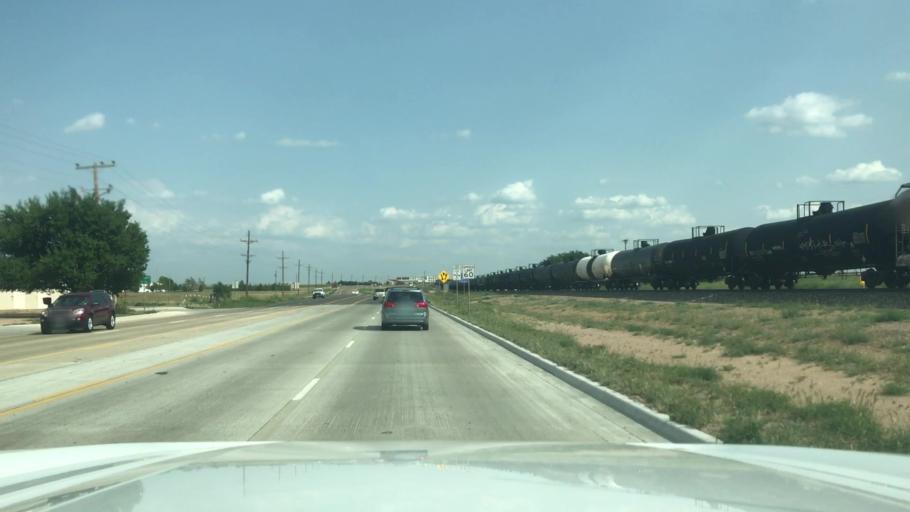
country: US
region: Texas
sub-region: Dallam County
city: Dalhart
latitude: 36.0481
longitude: -102.4965
